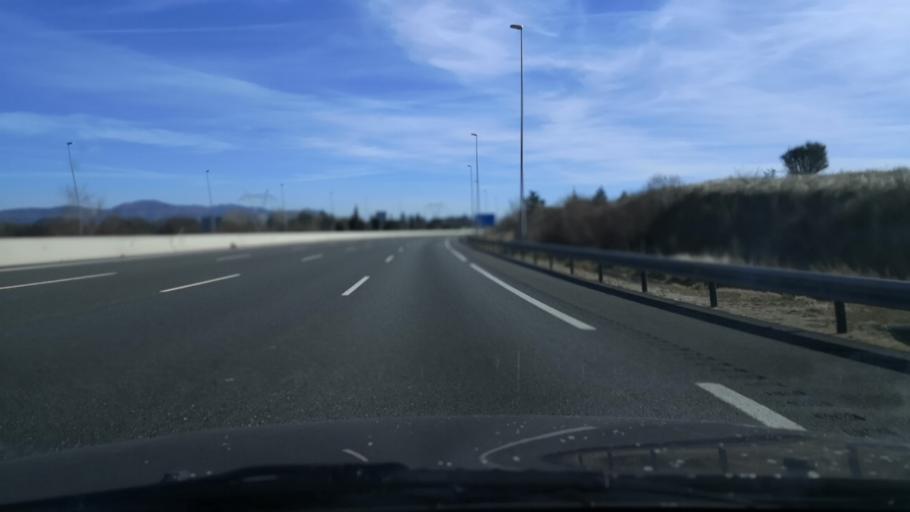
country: ES
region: Madrid
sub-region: Provincia de Madrid
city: Guadarrama
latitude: 40.6546
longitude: -4.0857
